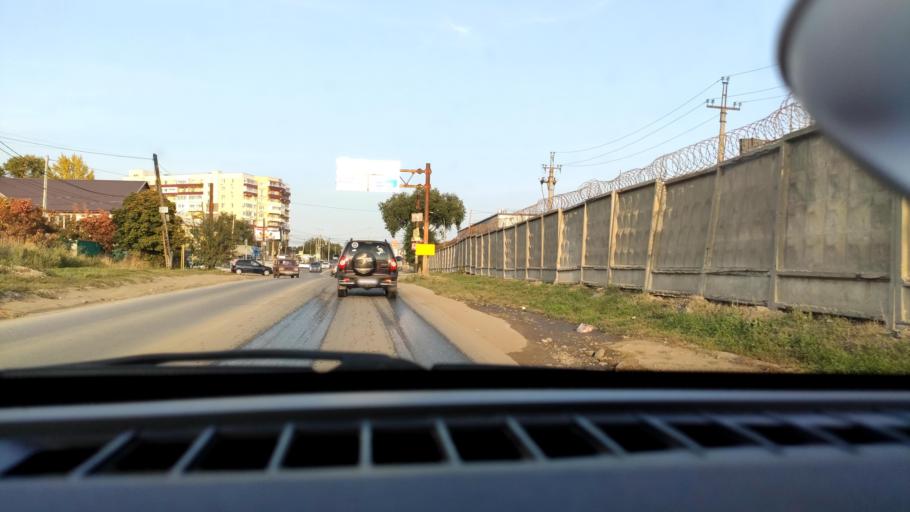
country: RU
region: Samara
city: Samara
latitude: 53.1785
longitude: 50.1893
